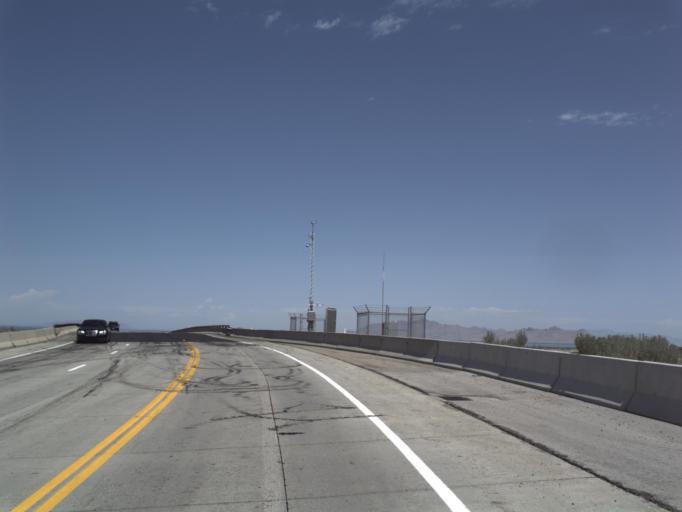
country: US
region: Utah
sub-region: Tooele County
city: Stansbury park
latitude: 40.6893
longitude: -112.2652
